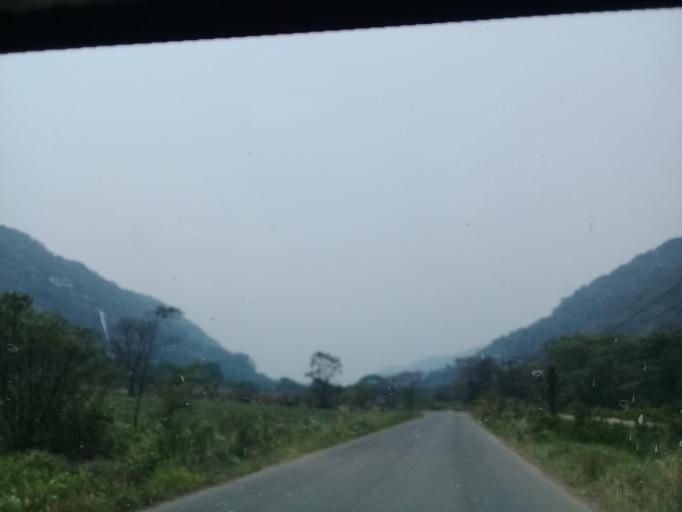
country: MX
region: Veracruz
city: Tezonapa
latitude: 18.6213
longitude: -96.7009
